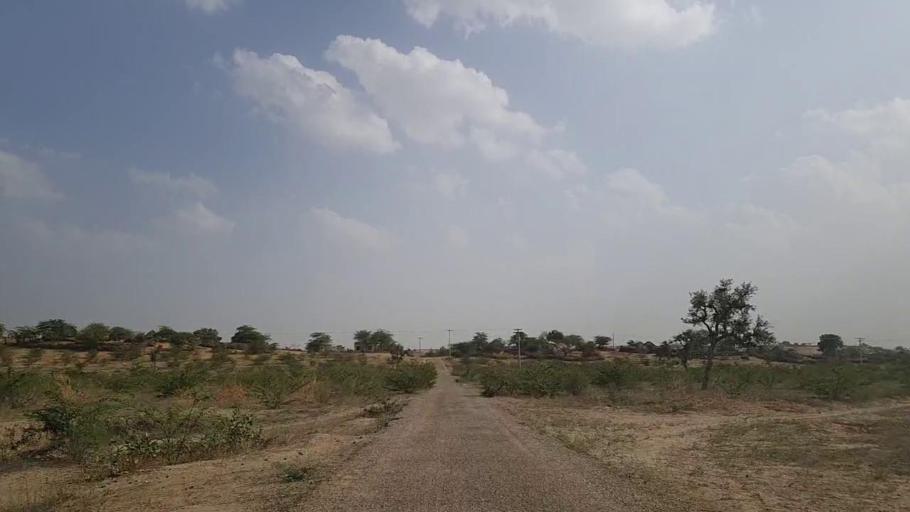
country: PK
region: Sindh
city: Islamkot
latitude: 24.8730
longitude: 70.1649
